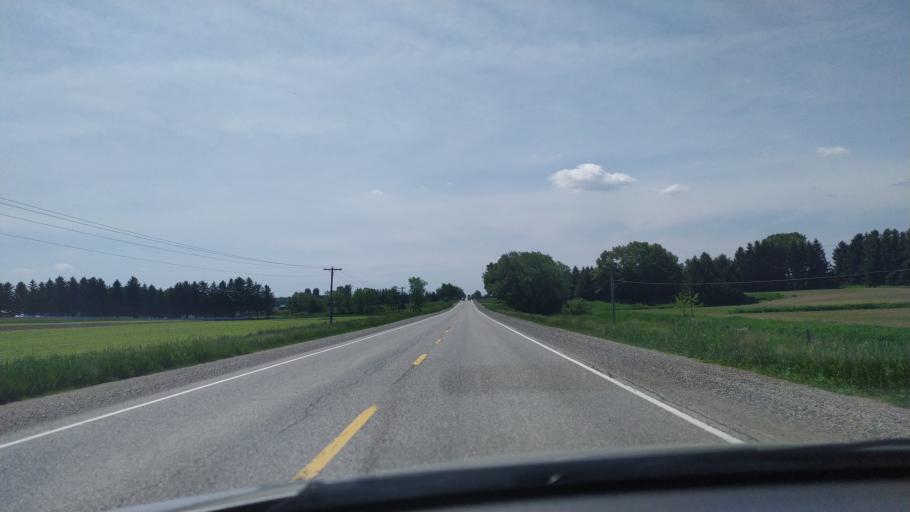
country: CA
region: Ontario
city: Dorchester
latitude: 43.1337
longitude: -81.0275
